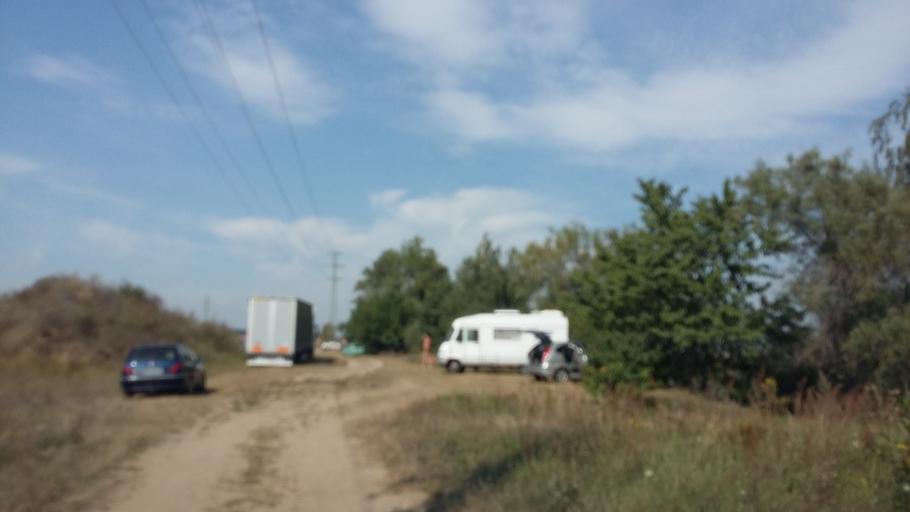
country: CZ
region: Central Bohemia
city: Veltruby
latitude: 50.0823
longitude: 15.1876
